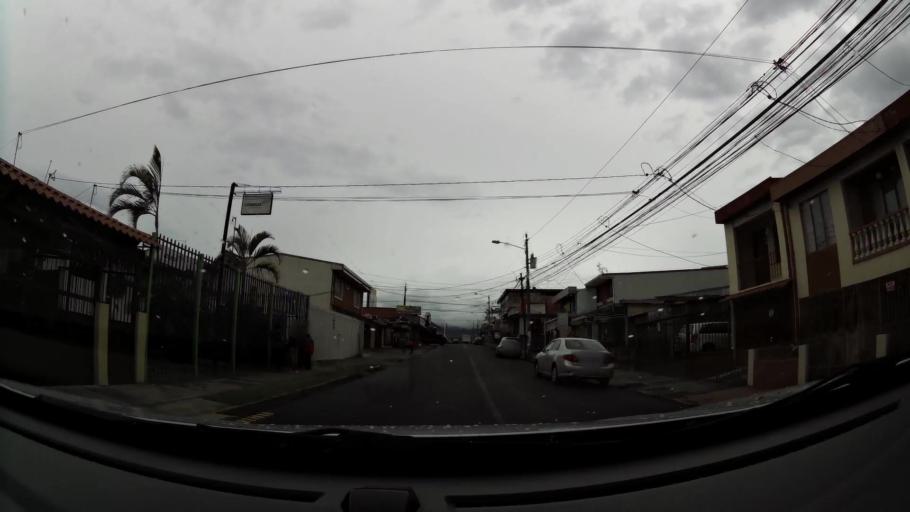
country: CR
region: San Jose
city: San Juan
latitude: 9.9608
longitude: -84.0775
